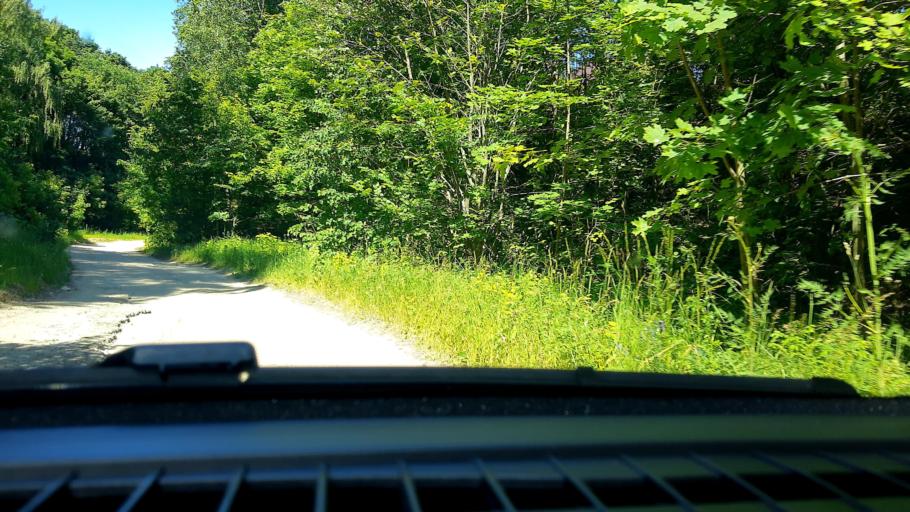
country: RU
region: Nizjnij Novgorod
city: Nizhniy Novgorod
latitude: 56.2245
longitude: 43.9153
